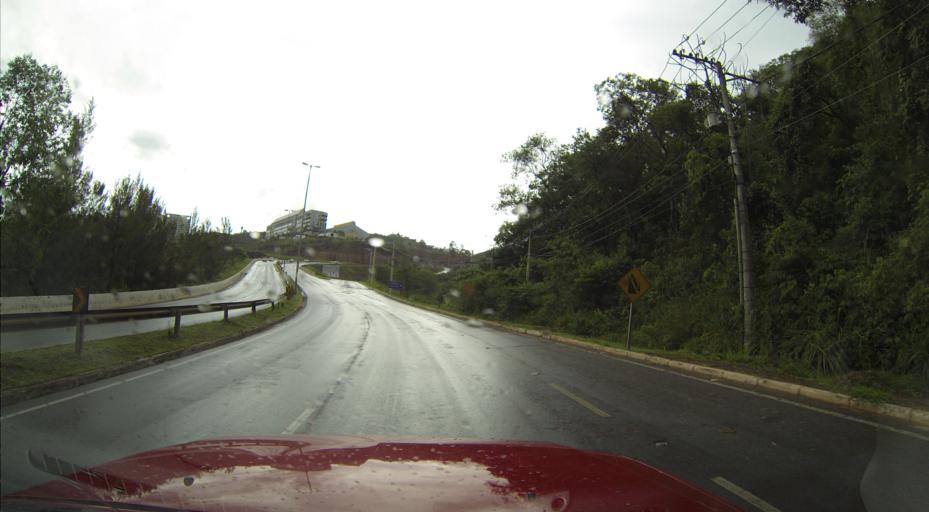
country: BR
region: Minas Gerais
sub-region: Belo Horizonte
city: Belo Horizonte
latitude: -19.9931
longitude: -43.9239
